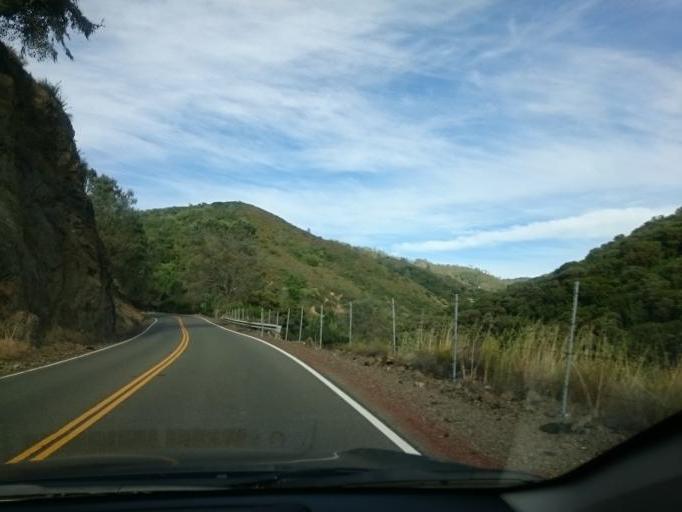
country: US
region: California
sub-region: Napa County
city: Yountville
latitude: 38.4867
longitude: -122.3002
